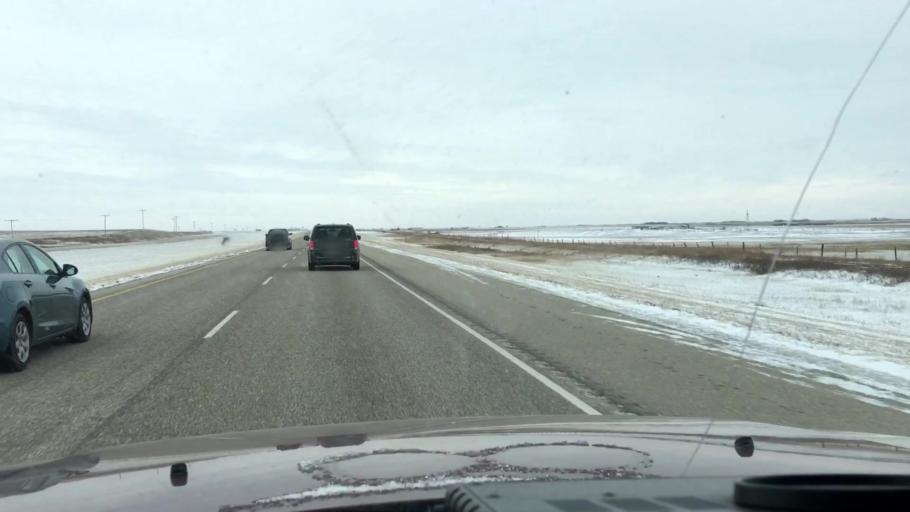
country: CA
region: Saskatchewan
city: Saskatoon
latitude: 51.5952
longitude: -106.3879
